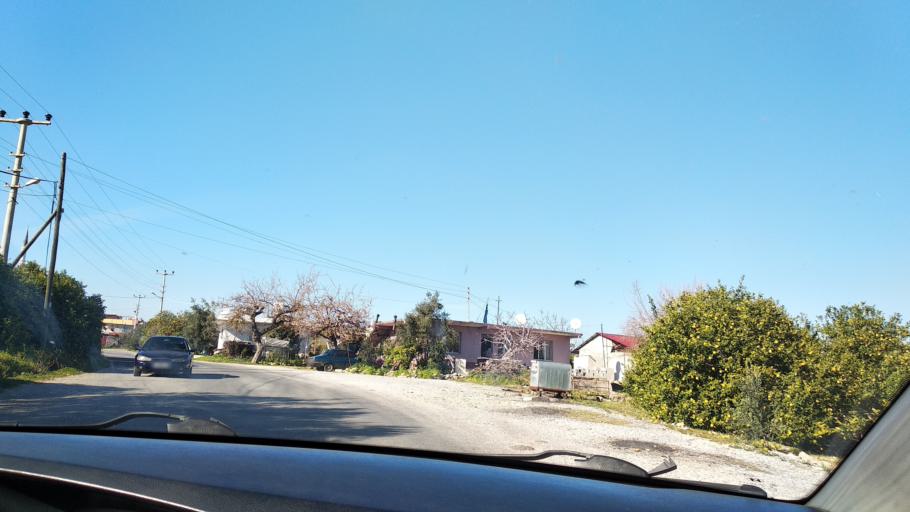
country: TR
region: Mersin
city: Tomuk
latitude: 36.6664
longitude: 34.3595
